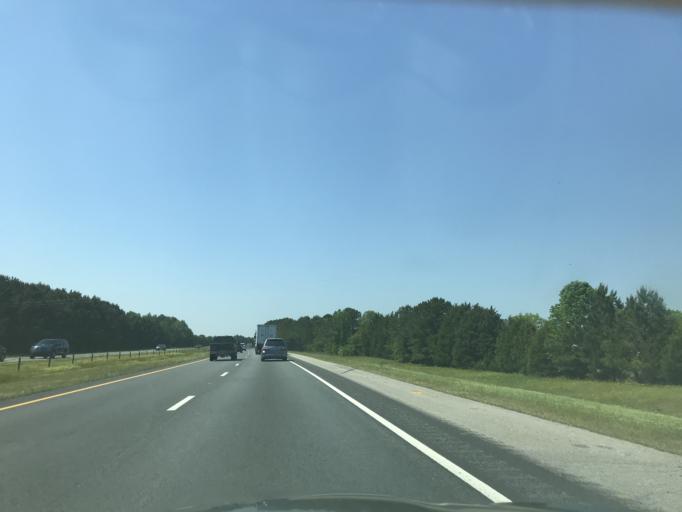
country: US
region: North Carolina
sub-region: Johnston County
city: Benson
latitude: 35.3679
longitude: -78.4941
